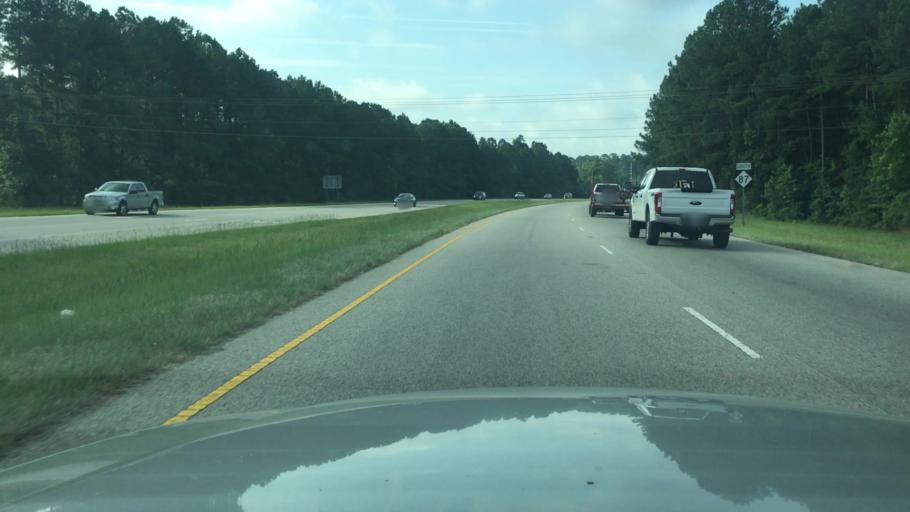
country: US
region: North Carolina
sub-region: Cumberland County
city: Vander
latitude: 34.9604
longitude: -78.8453
